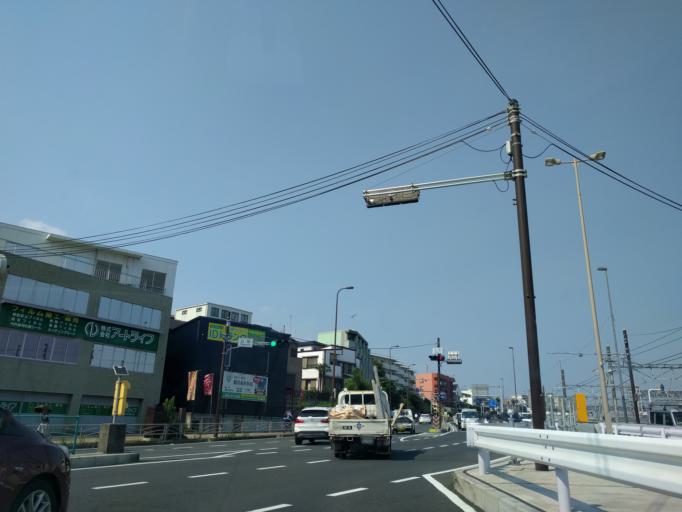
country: JP
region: Kanagawa
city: Yokohama
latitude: 35.4816
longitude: 139.6360
